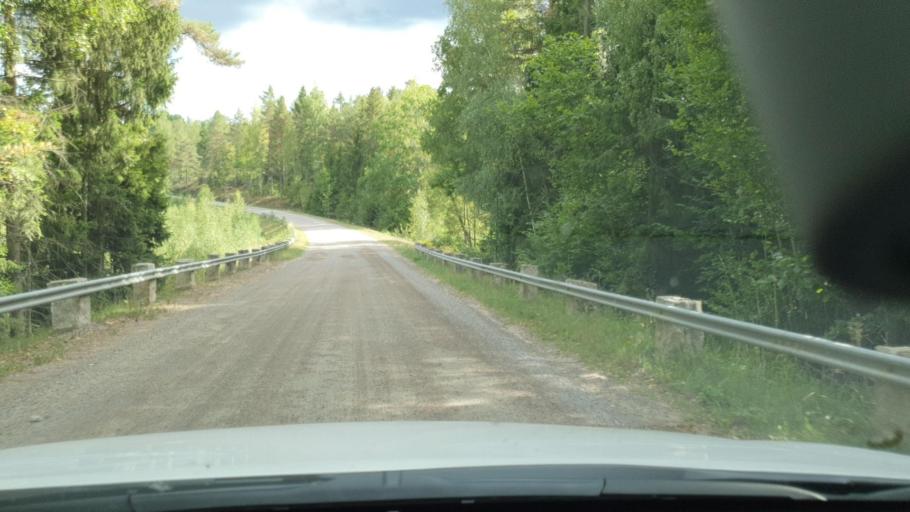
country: SE
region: Kalmar
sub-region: Vasterviks Kommun
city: Ankarsrum
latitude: 57.6947
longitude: 16.4653
